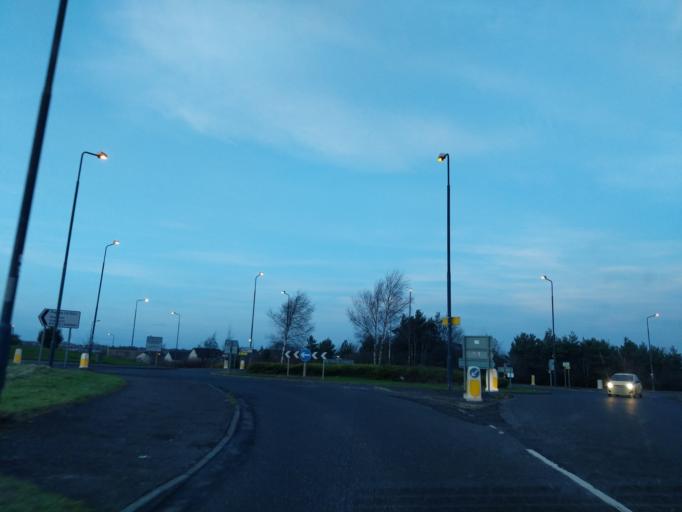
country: GB
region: Scotland
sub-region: Midlothian
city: Bonnyrigg
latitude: 55.8679
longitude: -3.0907
